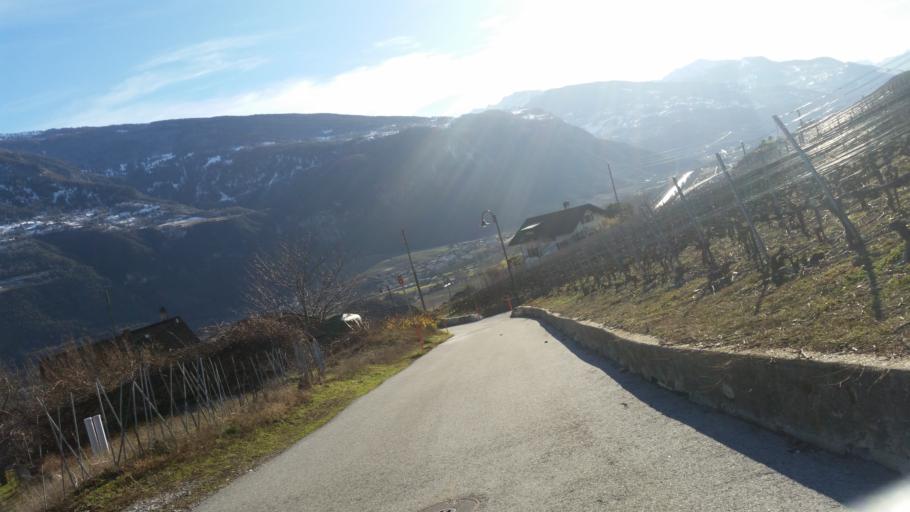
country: CH
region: Valais
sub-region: Sierre District
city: Chermignon-d'en Haut
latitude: 46.2727
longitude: 7.4642
